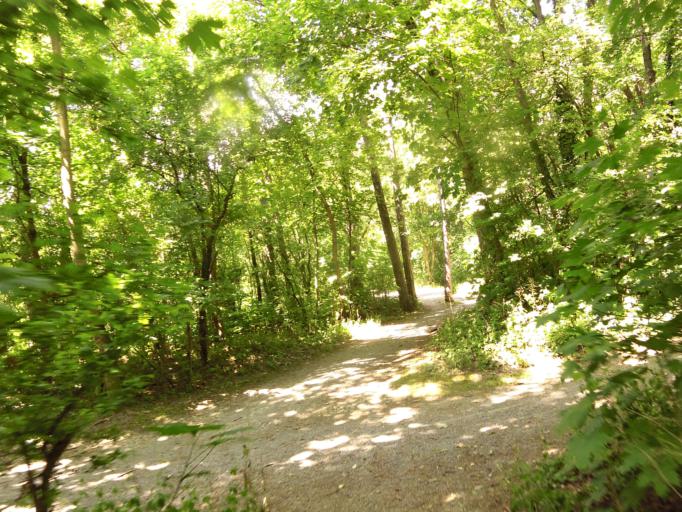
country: DE
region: Bavaria
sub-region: Regierungsbezirk Unterfranken
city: Wuerzburg
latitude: 49.7783
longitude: 9.9609
